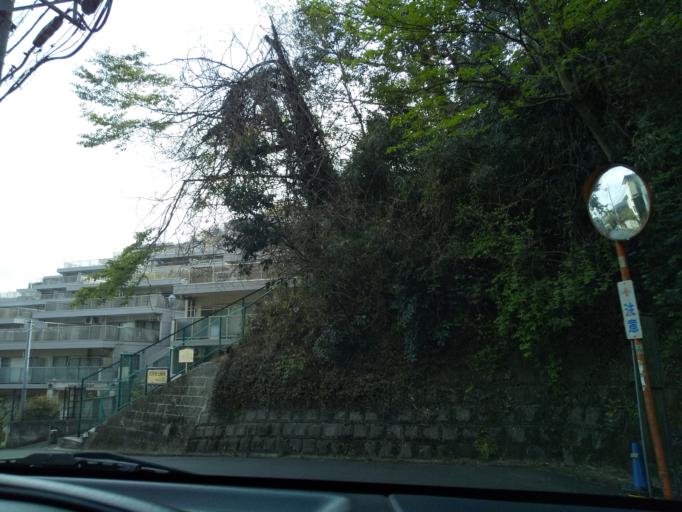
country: JP
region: Tokyo
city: Hino
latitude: 35.6551
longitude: 139.4284
